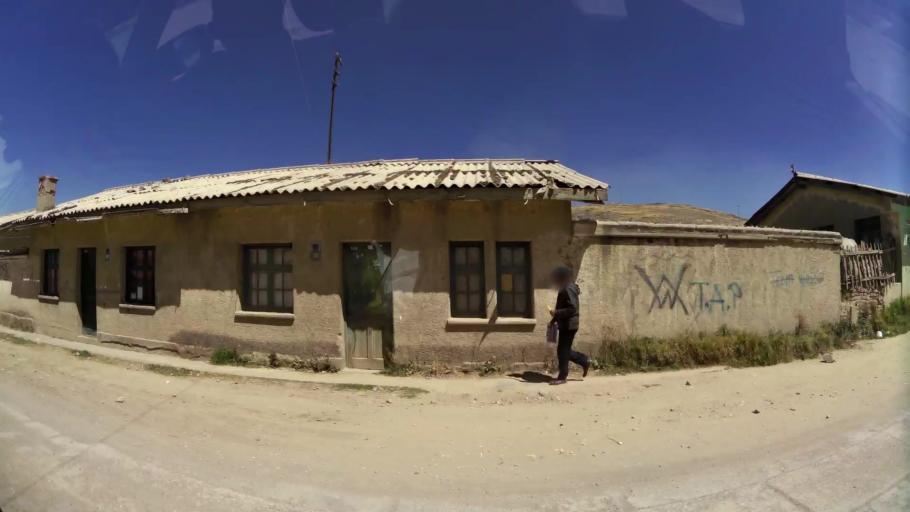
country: PE
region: Junin
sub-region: Provincia de Jauja
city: Jauja
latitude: -11.7822
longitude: -75.4951
